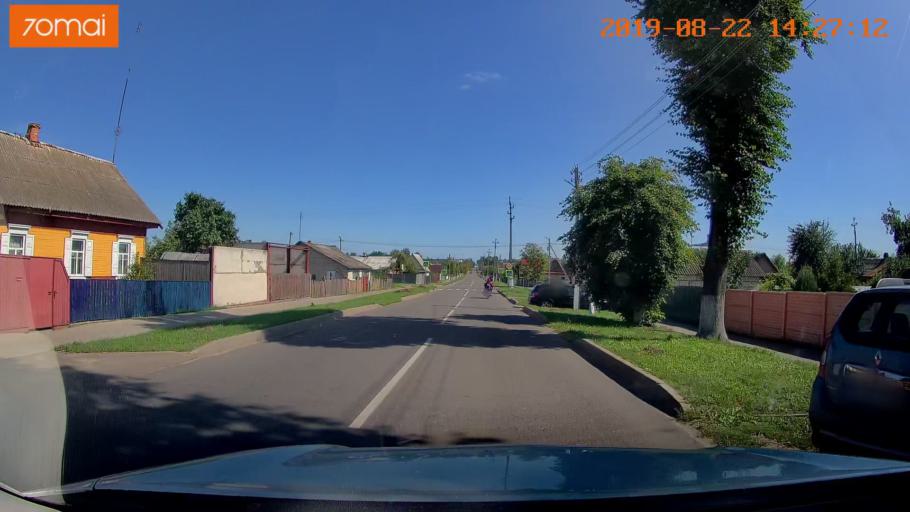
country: BY
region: Mogilev
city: Asipovichy
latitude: 53.2974
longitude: 28.6235
